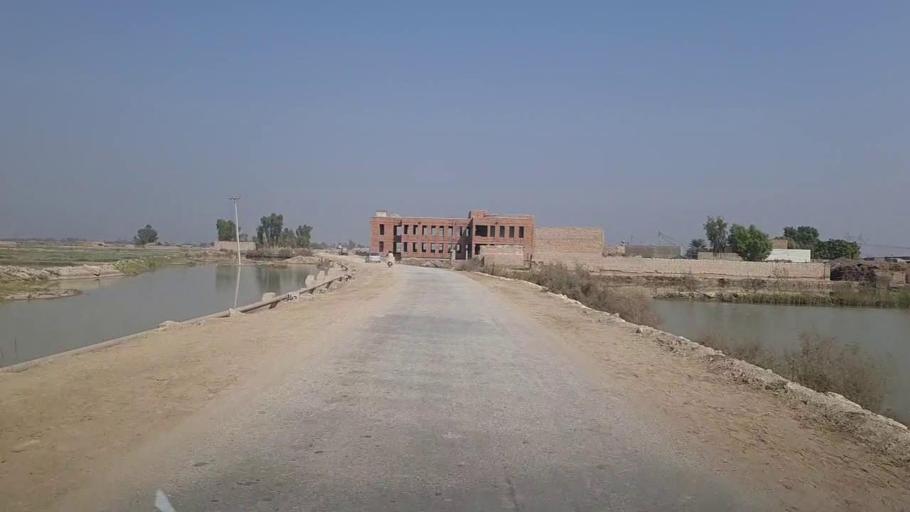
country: PK
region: Sindh
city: Kandhkot
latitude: 28.2283
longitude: 69.2090
